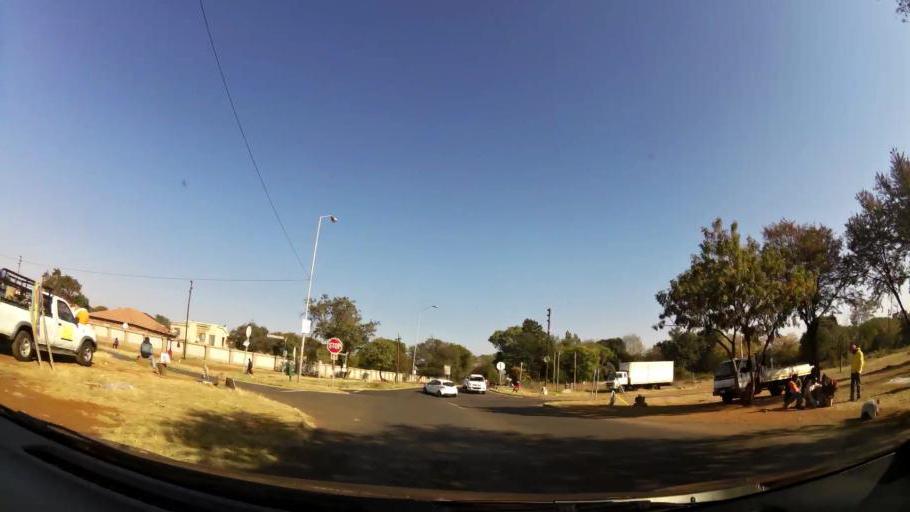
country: ZA
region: Gauteng
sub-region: City of Tshwane Metropolitan Municipality
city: Pretoria
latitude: -25.6669
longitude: 28.1324
